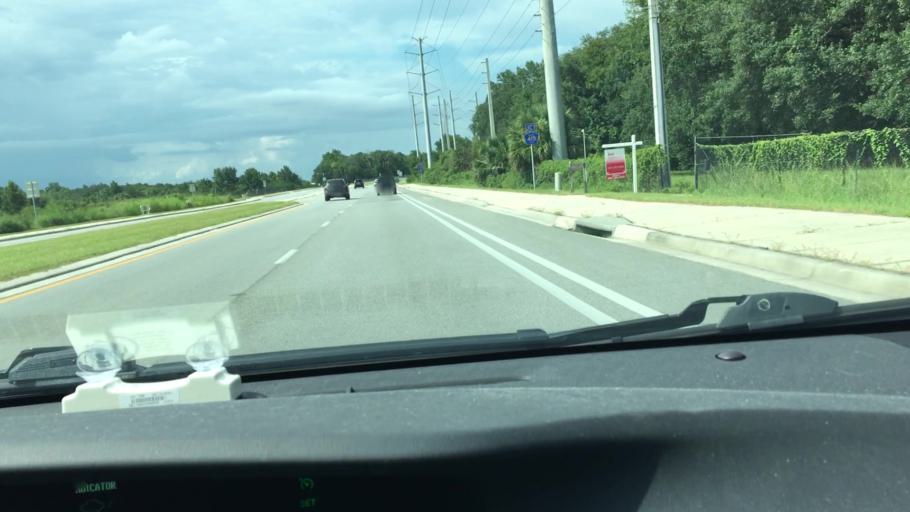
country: US
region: Florida
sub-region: Seminole County
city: Midway
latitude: 28.7959
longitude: -81.2189
